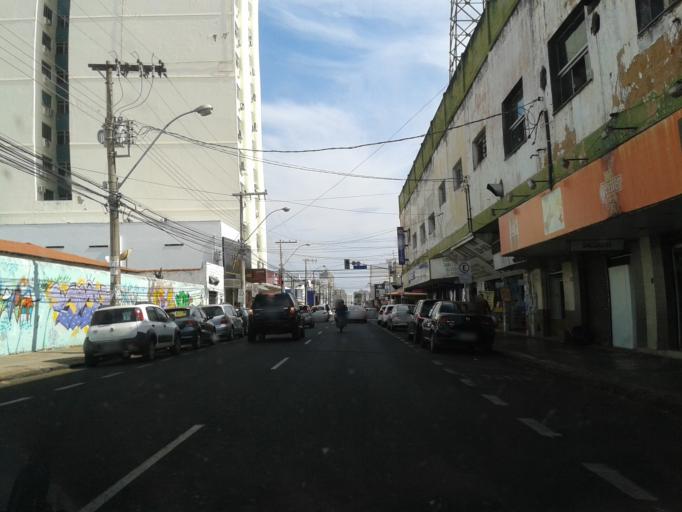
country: BR
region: Minas Gerais
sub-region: Uberlandia
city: Uberlandia
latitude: -18.9126
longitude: -48.2717
